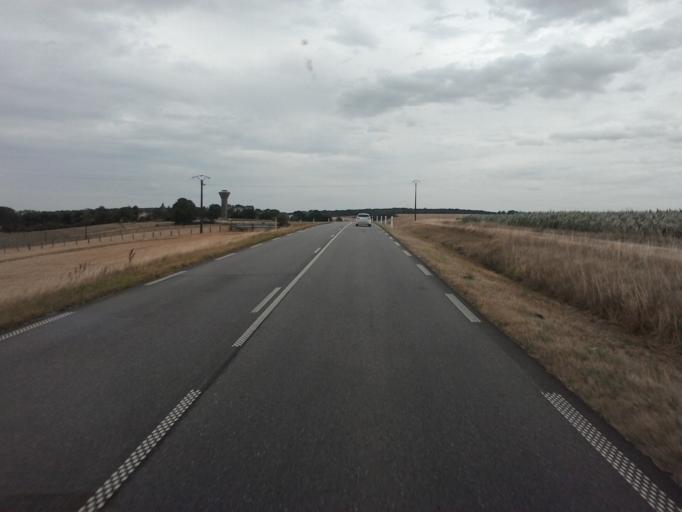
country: FR
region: Lorraine
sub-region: Departement de Meurthe-et-Moselle
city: Colombey-les-Belles
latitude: 48.4777
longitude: 5.8436
